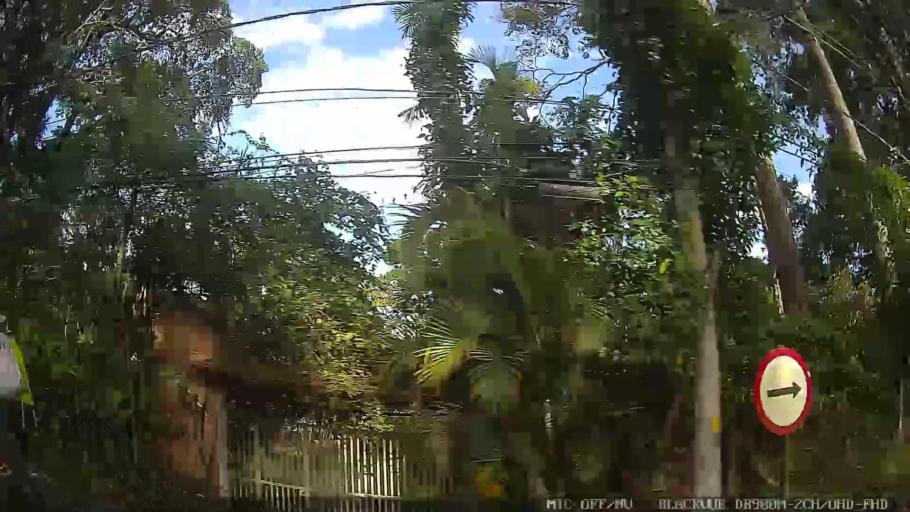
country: BR
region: Sao Paulo
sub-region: Mogi das Cruzes
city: Mogi das Cruzes
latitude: -23.5465
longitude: -46.1518
